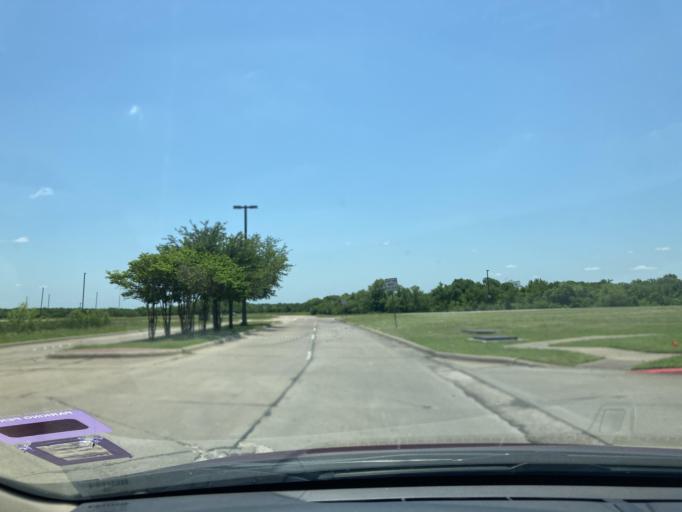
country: US
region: Texas
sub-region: Navarro County
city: Corsicana
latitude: 32.0661
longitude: -96.4483
